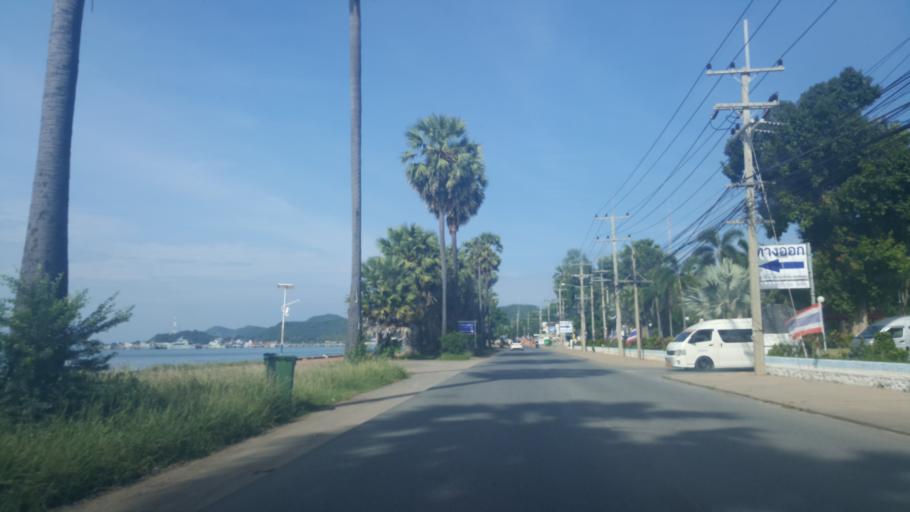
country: TH
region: Chon Buri
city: Sattahip
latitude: 12.6616
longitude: 100.9101
